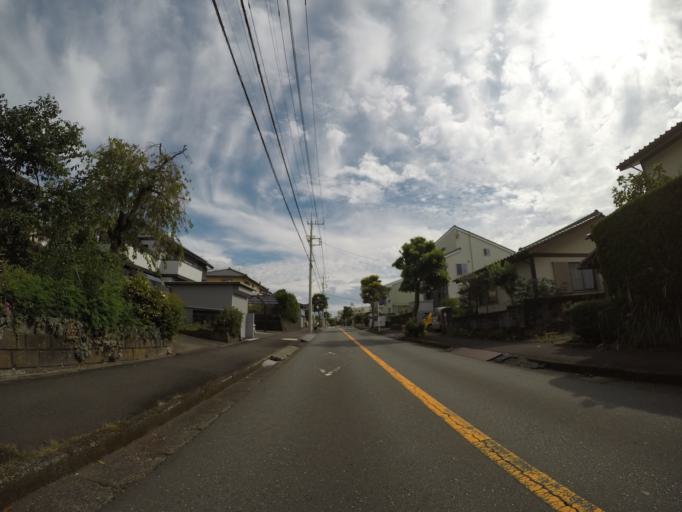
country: JP
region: Shizuoka
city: Fuji
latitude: 35.1858
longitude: 138.7113
